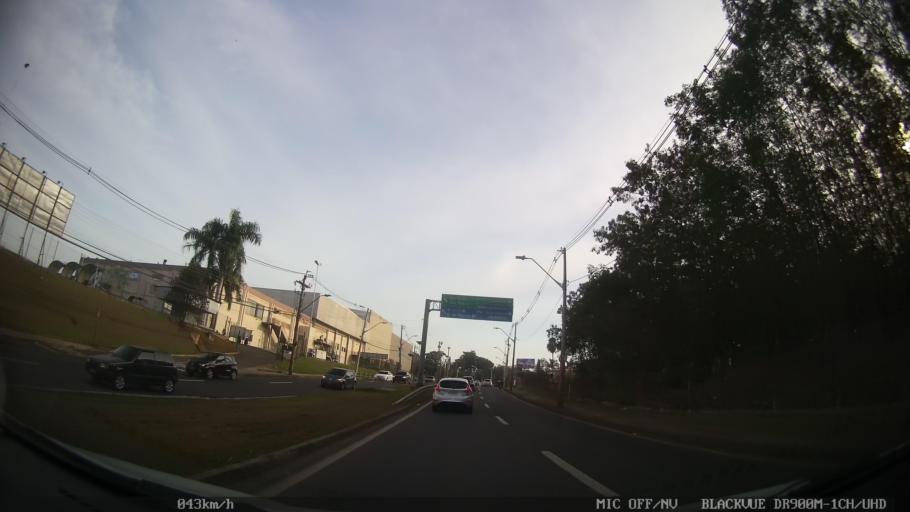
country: BR
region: Sao Paulo
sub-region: Piracicaba
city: Piracicaba
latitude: -22.7042
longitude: -47.6477
